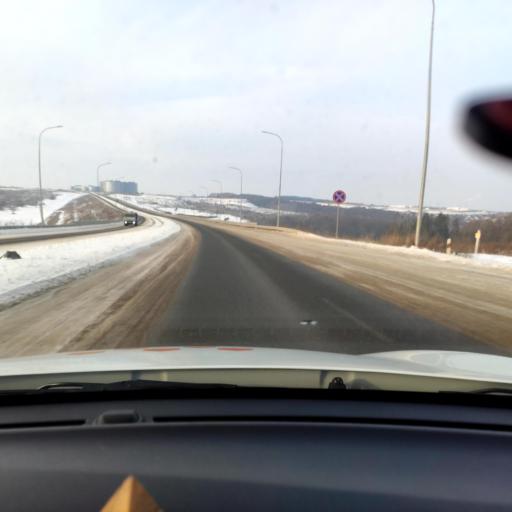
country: RU
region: Tatarstan
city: Sviyazhsk
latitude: 55.7438
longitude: 48.7730
